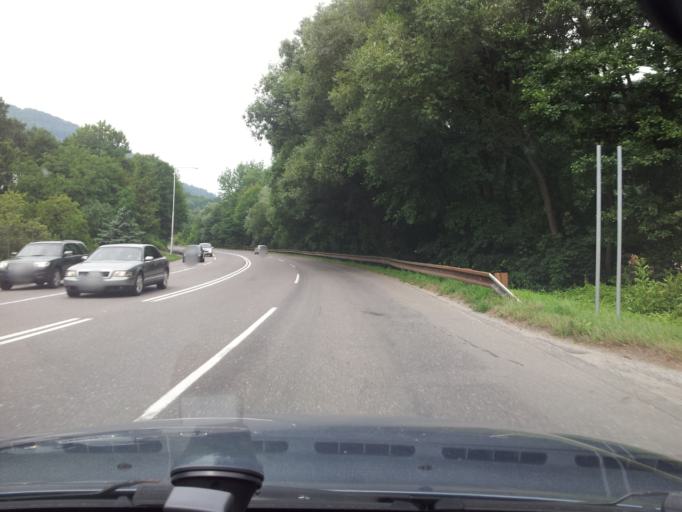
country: SK
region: Banskobystricky
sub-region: Okres Banska Bystrica
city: Banska Bystrica
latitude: 48.7783
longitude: 19.1275
